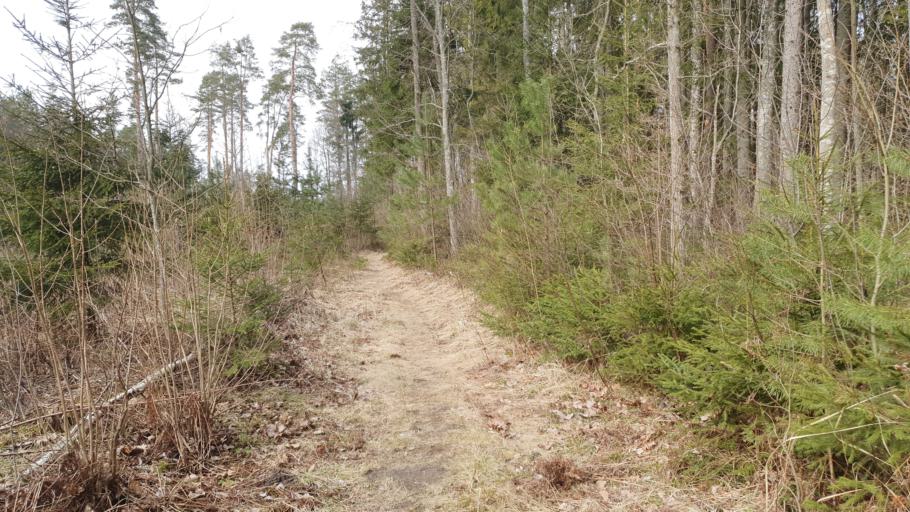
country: LV
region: Beverina
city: Murmuiza
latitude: 57.5491
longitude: 25.5199
